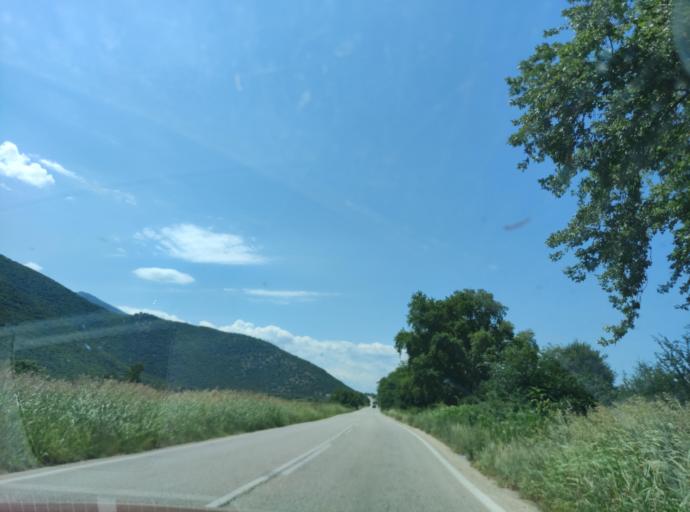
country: GR
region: East Macedonia and Thrace
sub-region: Nomos Kavalas
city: Palaiochori
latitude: 40.9674
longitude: 24.1781
